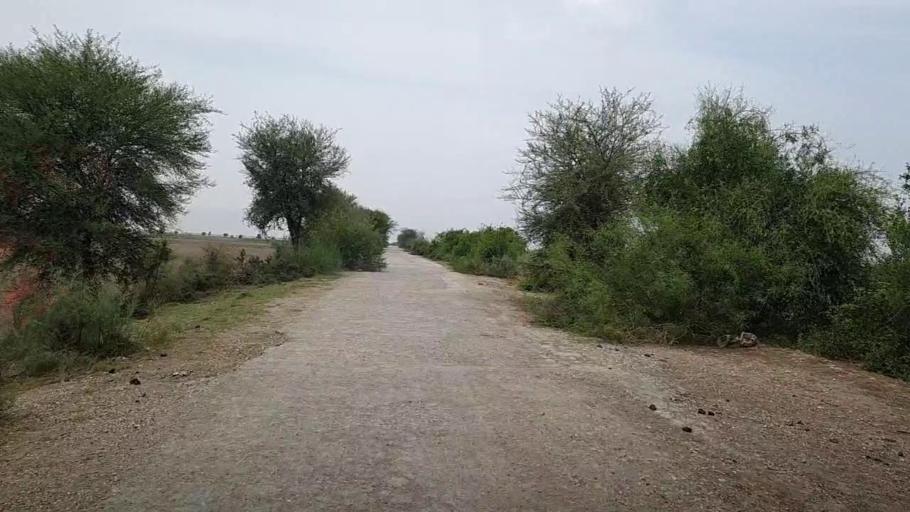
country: PK
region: Sindh
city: Sann
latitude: 26.2042
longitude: 67.9694
